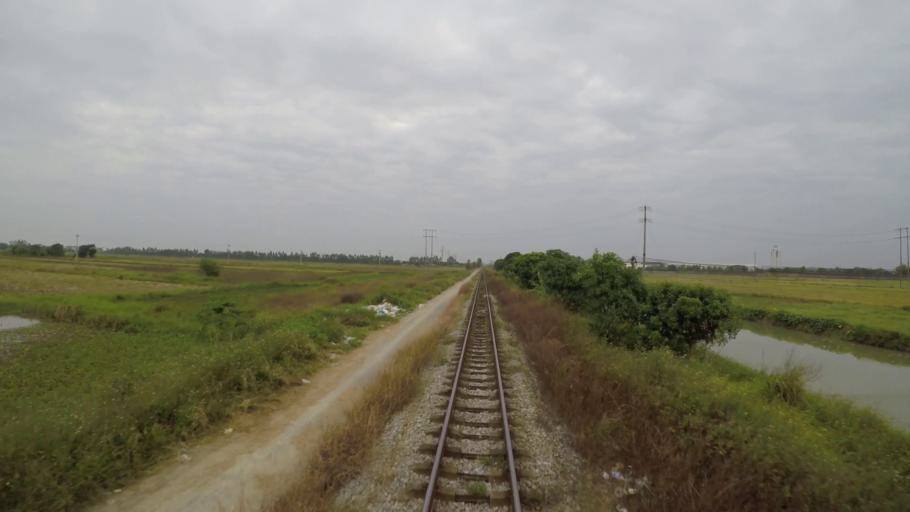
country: VN
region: Hai Duong
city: Lai Cach
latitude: 20.9480
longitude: 106.2558
